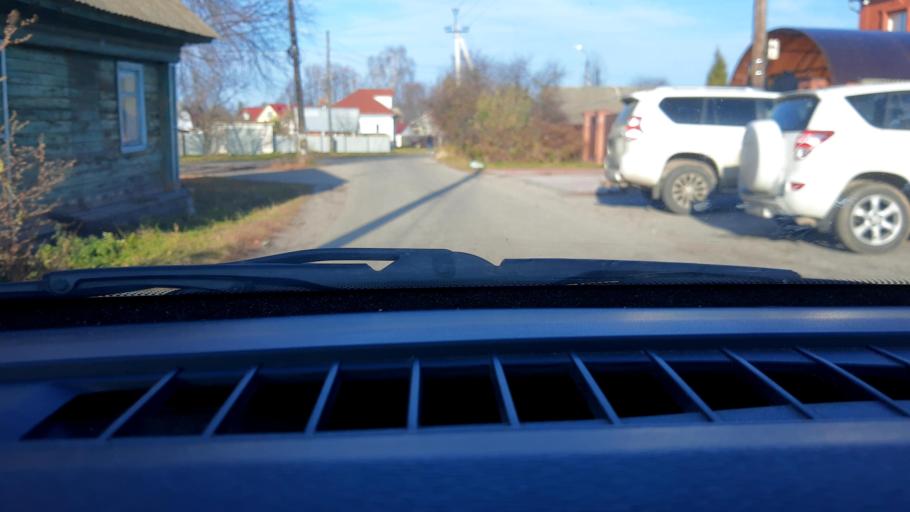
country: RU
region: Nizjnij Novgorod
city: Gorodets
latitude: 56.6384
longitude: 43.4700
